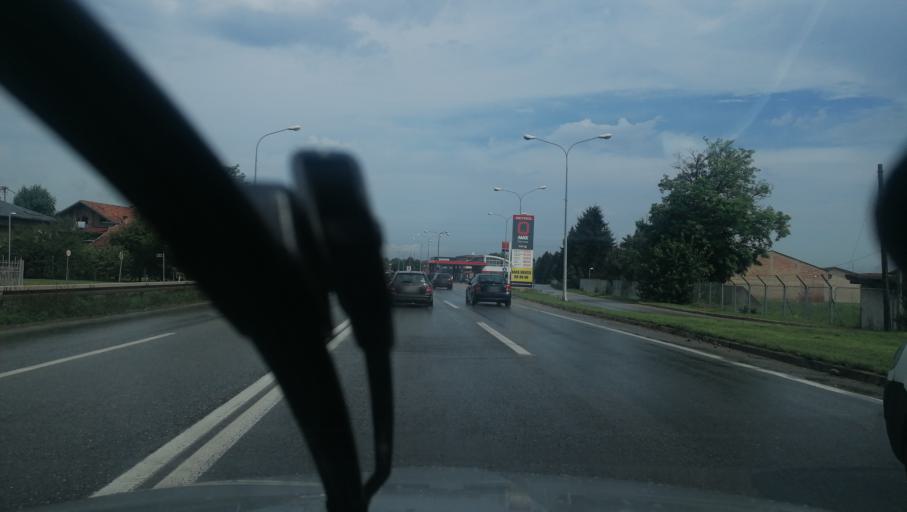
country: BA
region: Republika Srpska
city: Banja Luka
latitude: 44.8017
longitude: 17.1986
